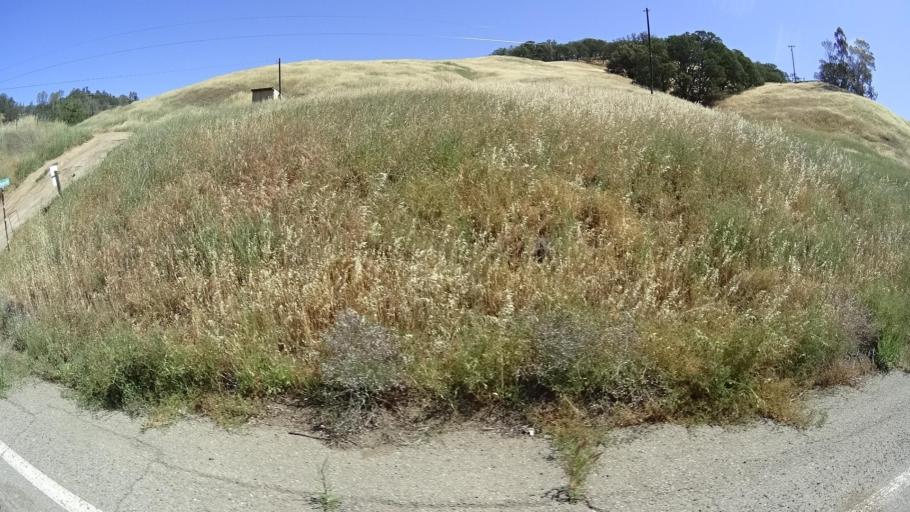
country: US
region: California
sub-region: Lake County
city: Lower Lake
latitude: 38.8982
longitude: -122.5558
